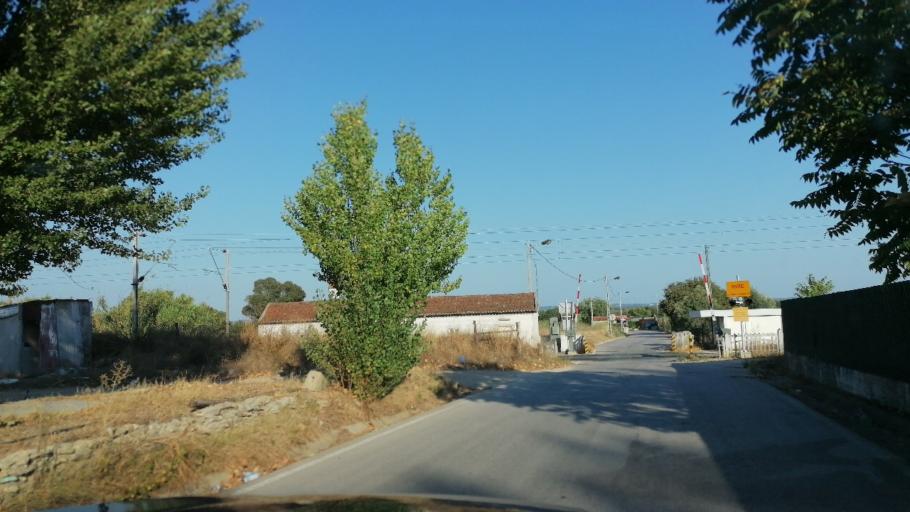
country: PT
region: Santarem
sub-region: Santarem
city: Santarem
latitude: 39.2548
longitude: -8.6732
